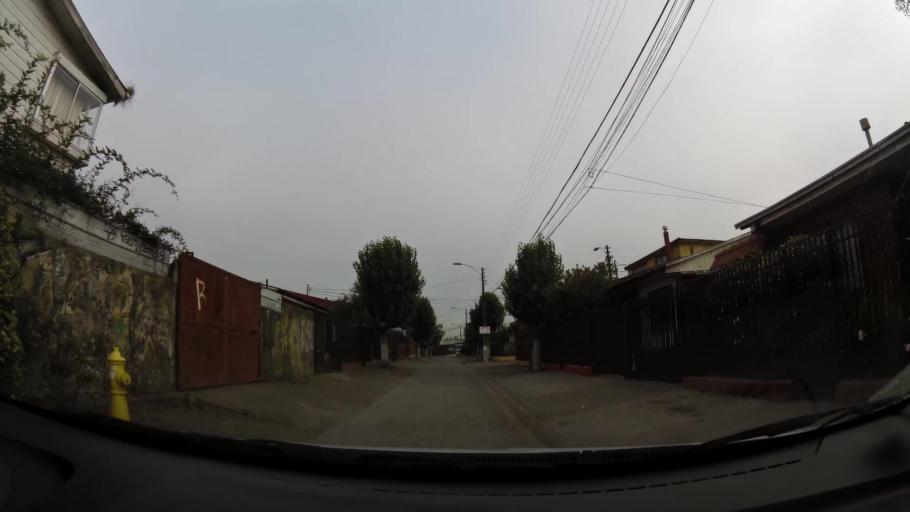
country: CL
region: Biobio
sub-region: Provincia de Concepcion
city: Concepcion
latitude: -36.8019
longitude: -73.0818
